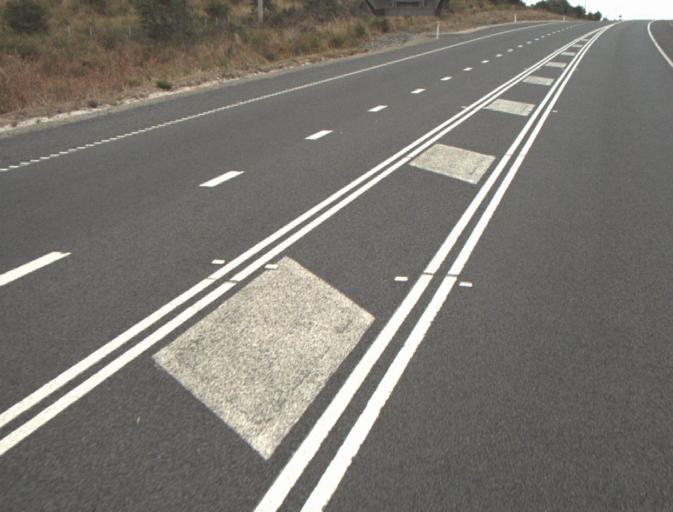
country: AU
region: Tasmania
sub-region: Launceston
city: Mayfield
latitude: -41.2596
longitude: 147.0267
